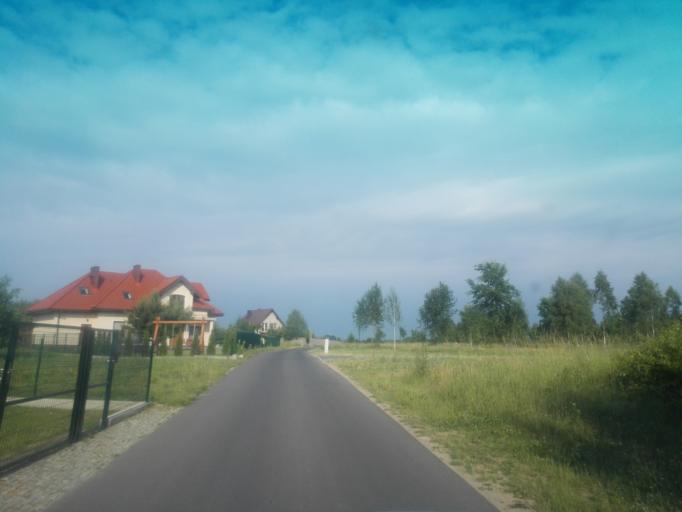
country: PL
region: Silesian Voivodeship
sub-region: Powiat czestochowski
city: Mstow
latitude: 50.8318
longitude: 19.3053
